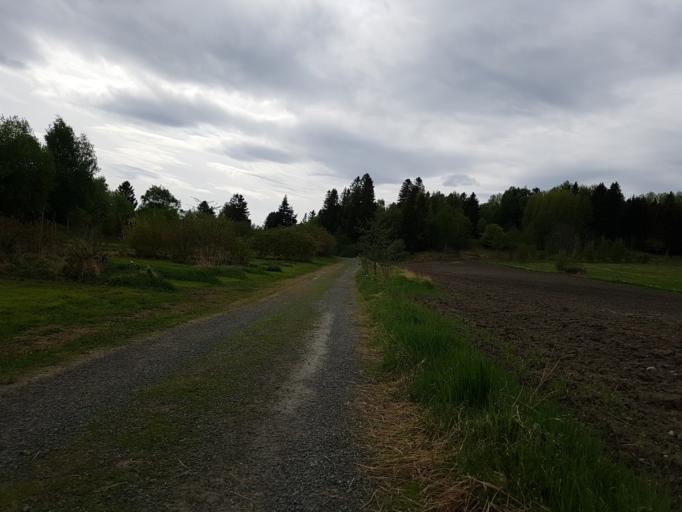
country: NO
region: Nord-Trondelag
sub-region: Levanger
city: Levanger
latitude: 63.7442
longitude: 11.2727
